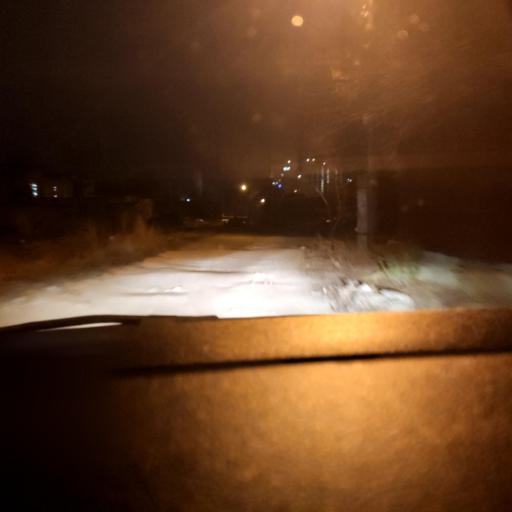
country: RU
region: Voronezj
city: Voronezh
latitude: 51.6717
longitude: 39.1438
